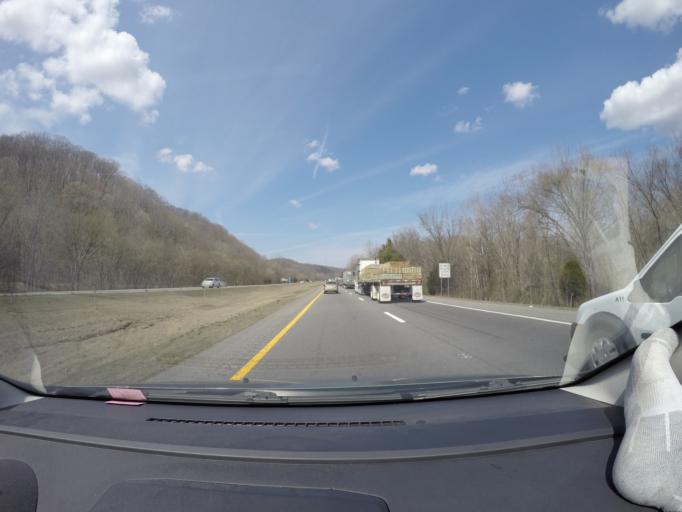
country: US
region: Tennessee
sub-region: Robertson County
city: Ridgetop
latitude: 36.3060
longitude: -86.8162
